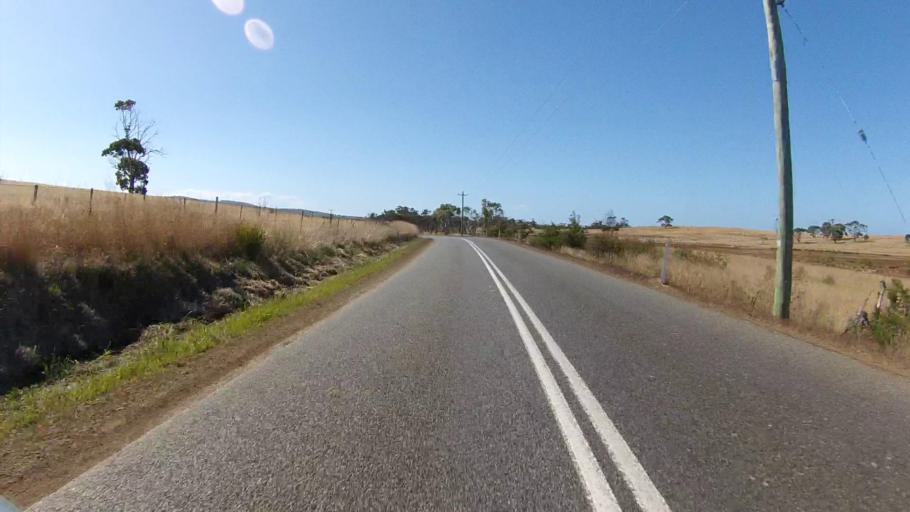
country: AU
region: Tasmania
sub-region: Sorell
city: Sorell
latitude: -42.2774
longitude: 148.0036
